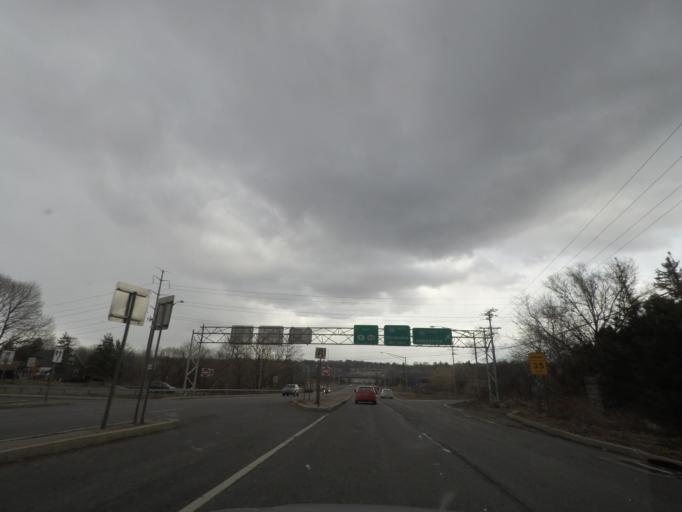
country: US
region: New York
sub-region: Onondaga County
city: East Syracuse
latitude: 43.0343
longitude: -76.0636
